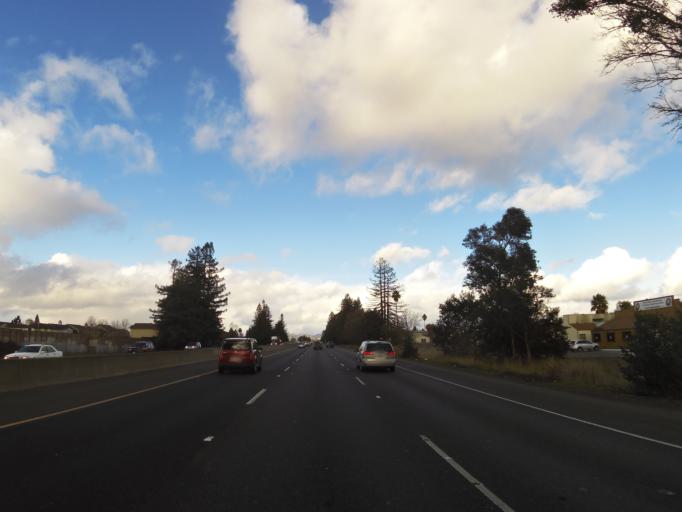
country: US
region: California
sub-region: Sonoma County
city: Roseland
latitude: 38.3948
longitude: -122.7161
